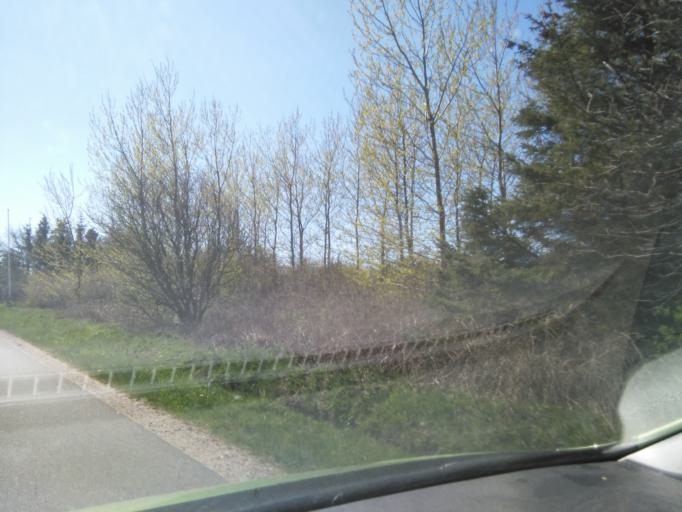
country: DK
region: South Denmark
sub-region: Varde Kommune
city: Oksbol
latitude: 55.5684
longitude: 8.2249
